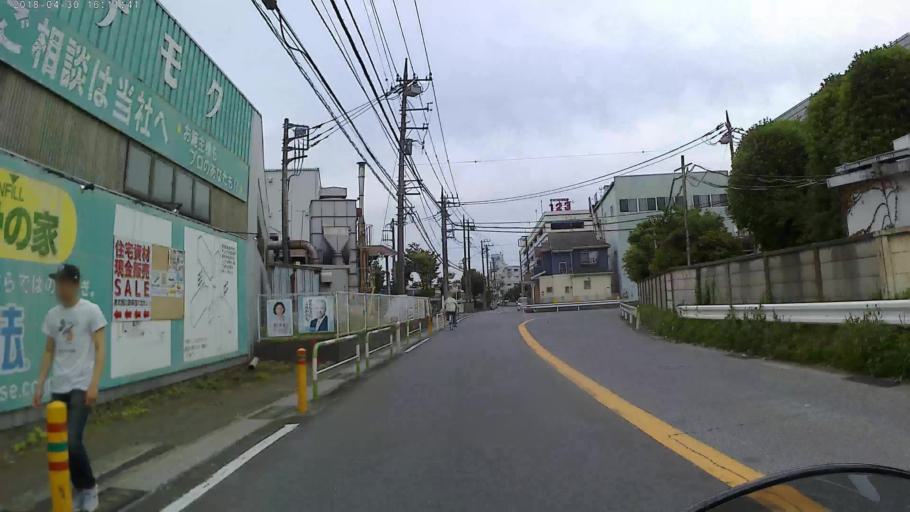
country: JP
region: Kanagawa
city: Minami-rinkan
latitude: 35.5003
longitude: 139.4284
